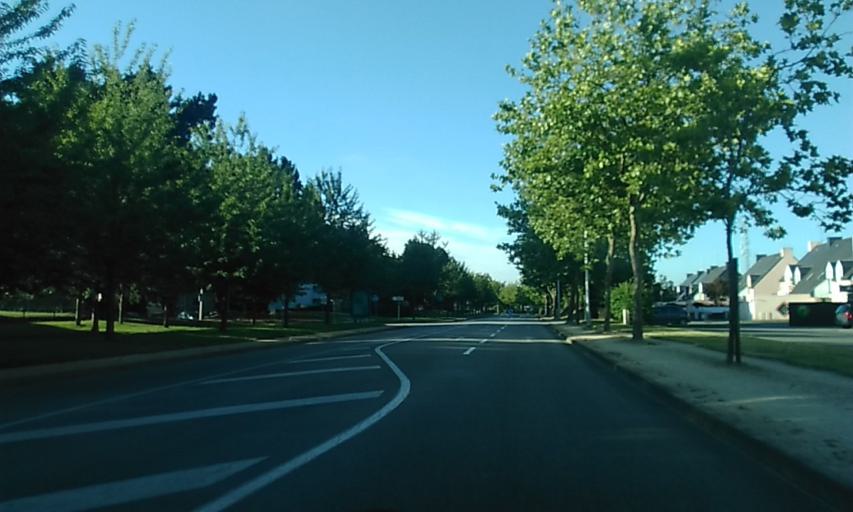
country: FR
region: Brittany
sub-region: Departement du Morbihan
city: Vannes
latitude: 47.6558
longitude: -2.7826
